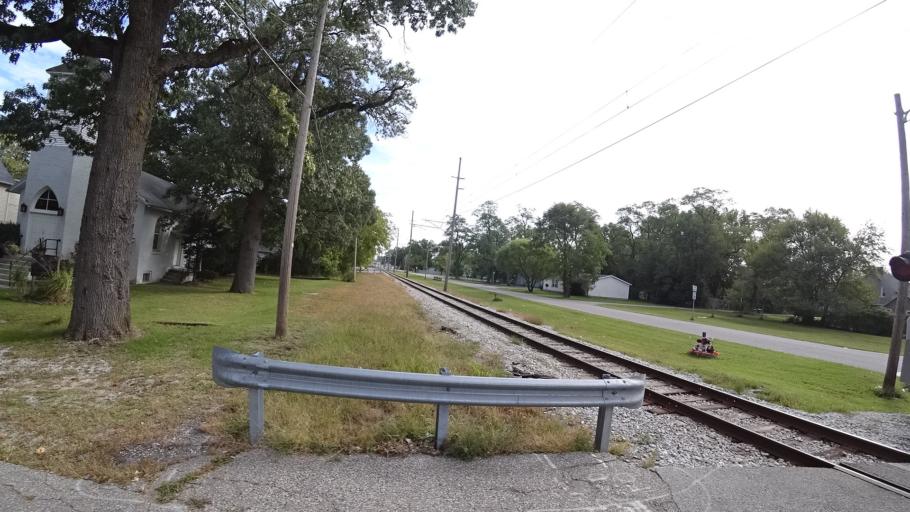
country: US
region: Indiana
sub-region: LaPorte County
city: Michigan City
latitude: 41.7133
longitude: -86.8776
